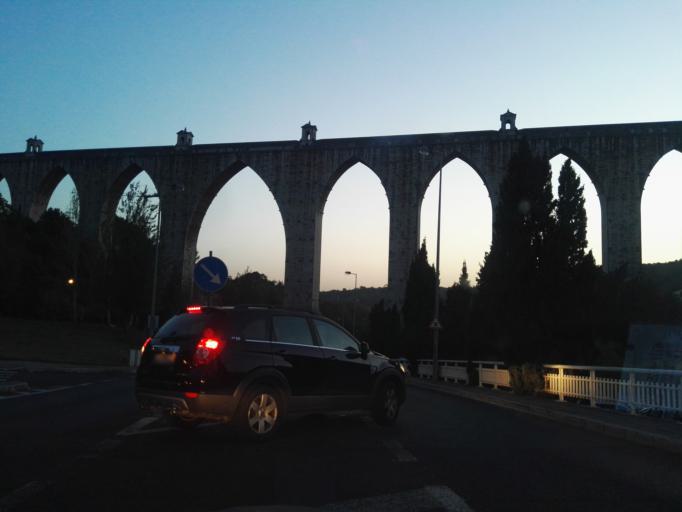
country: PT
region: Lisbon
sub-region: Lisbon
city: Lisbon
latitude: 38.7305
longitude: -9.1687
